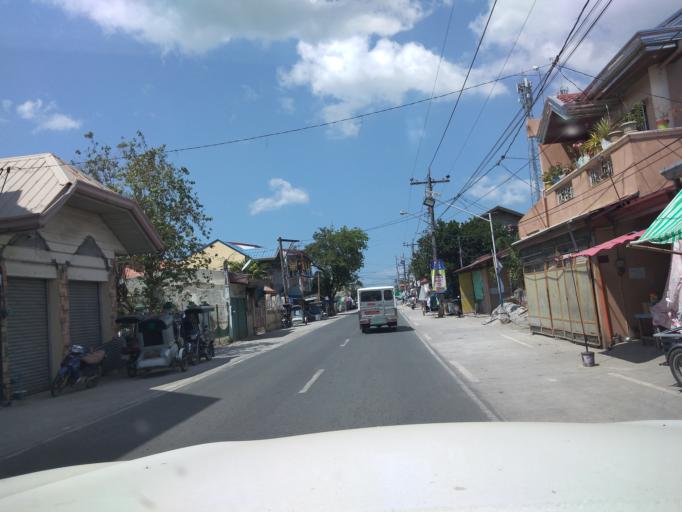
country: PH
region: Central Luzon
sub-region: Province of Pampanga
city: Bahay Pare
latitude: 15.0264
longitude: 120.8827
